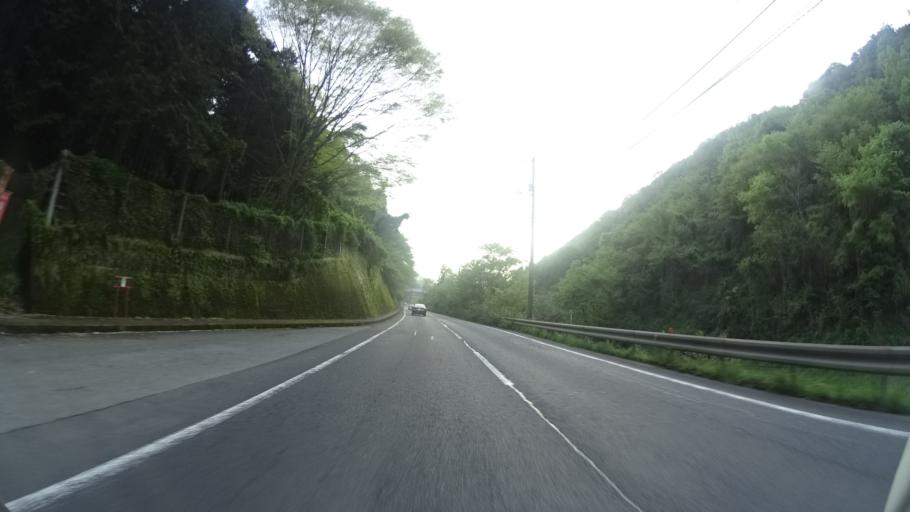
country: JP
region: Tokushima
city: Ikedacho
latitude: 34.0003
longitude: 133.6987
